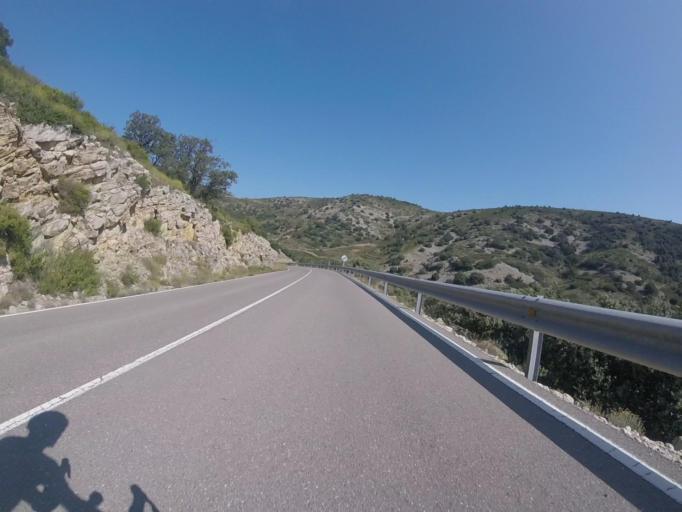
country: ES
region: Valencia
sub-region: Provincia de Castello
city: Benafigos
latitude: 40.2651
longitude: -0.2323
